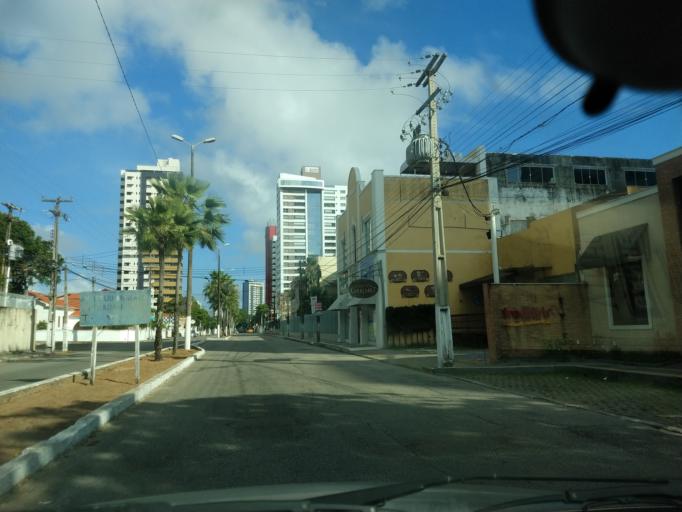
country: BR
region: Rio Grande do Norte
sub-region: Natal
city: Natal
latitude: -5.7852
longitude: -35.1970
